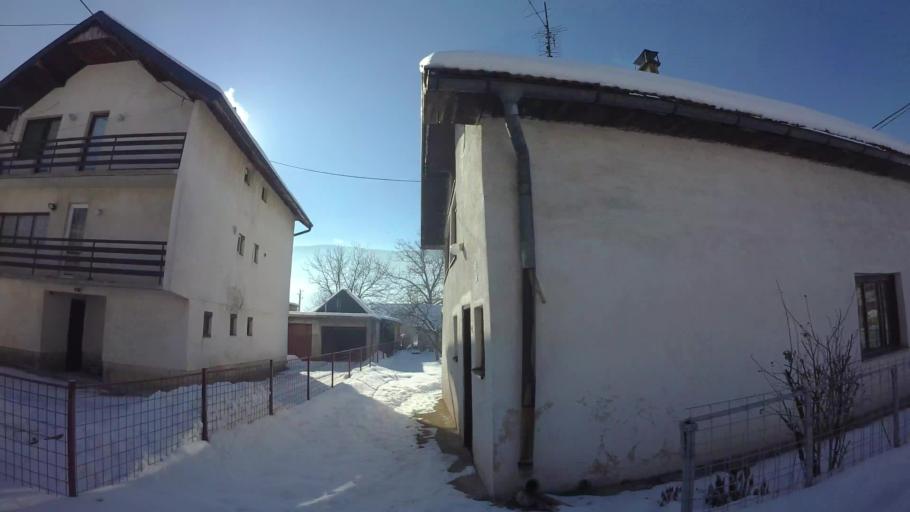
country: BA
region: Federation of Bosnia and Herzegovina
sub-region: Kanton Sarajevo
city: Sarajevo
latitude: 43.7940
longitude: 18.3461
